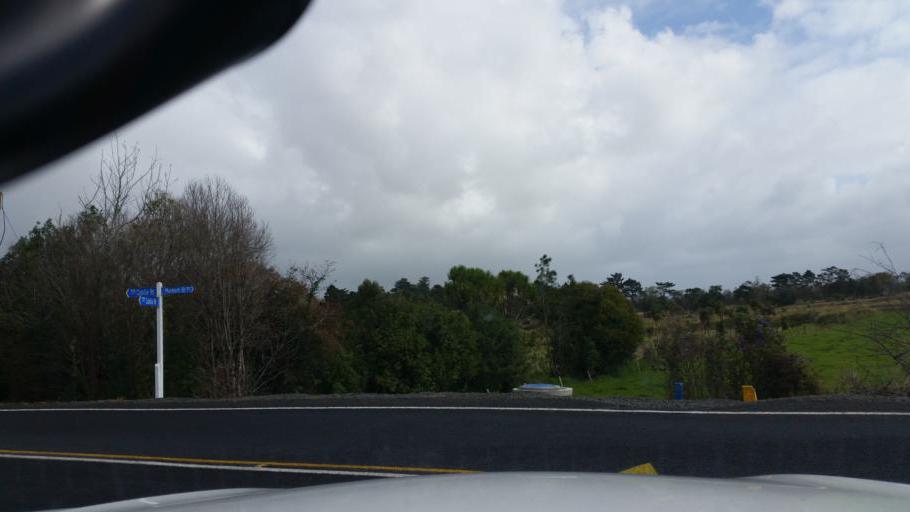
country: NZ
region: Northland
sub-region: Kaipara District
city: Dargaville
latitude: -35.9522
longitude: 173.8560
